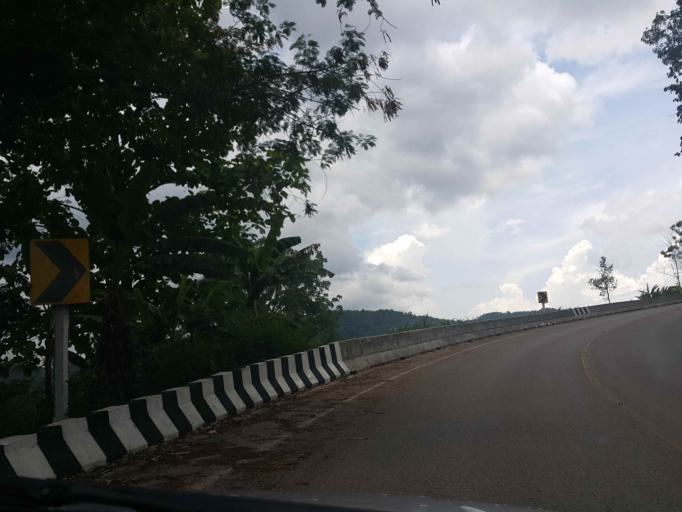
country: TH
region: Lampang
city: Ngao
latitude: 18.9291
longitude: 100.0933
